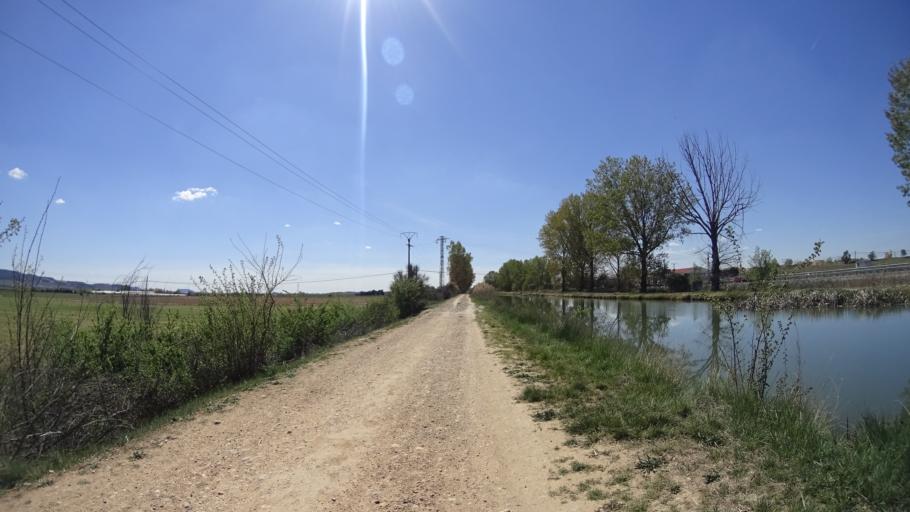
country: ES
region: Castille and Leon
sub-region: Provincia de Valladolid
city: Cabezon
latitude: 41.7386
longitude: -4.6664
